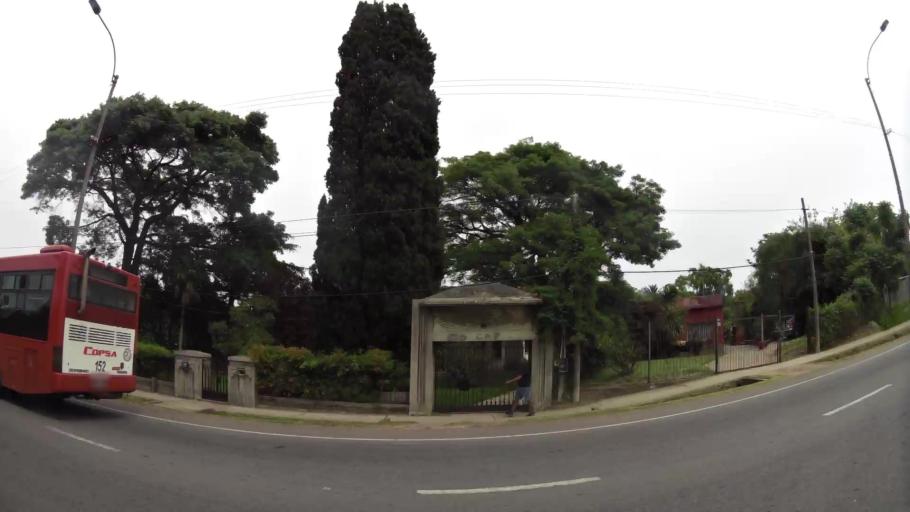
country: UY
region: Canelones
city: La Paz
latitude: -34.7910
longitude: -56.2243
